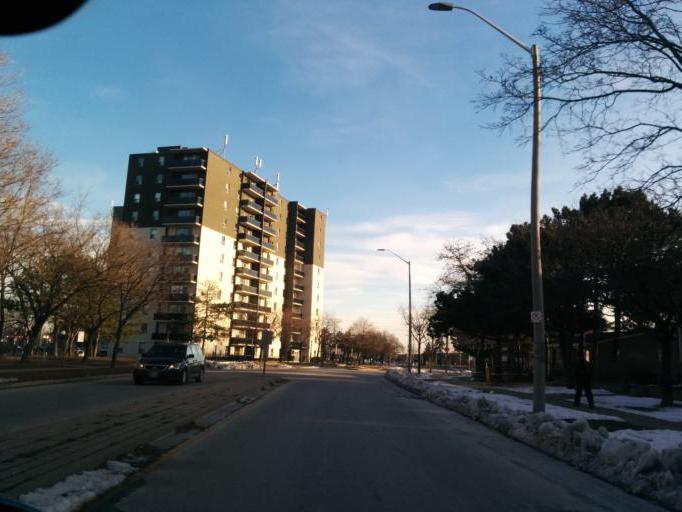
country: CA
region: Ontario
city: Etobicoke
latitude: 43.6087
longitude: -79.5887
